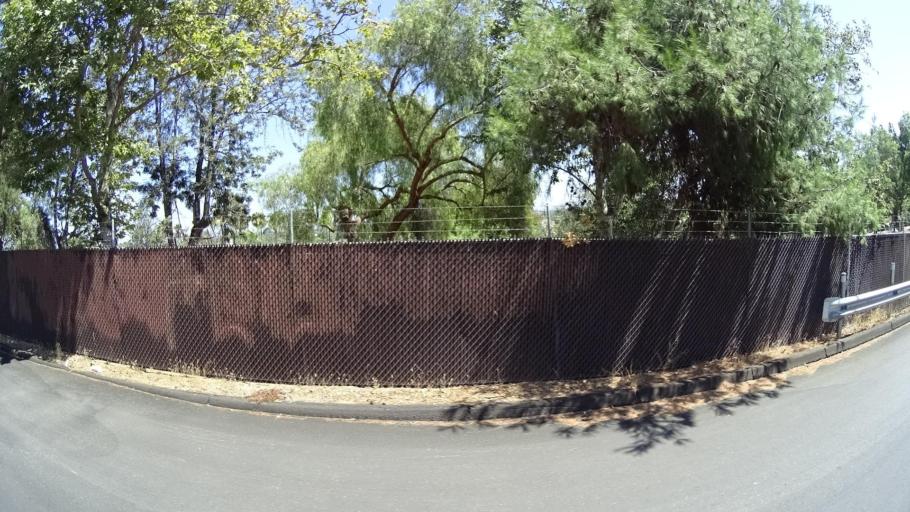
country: US
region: California
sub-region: San Diego County
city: Fallbrook
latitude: 33.3623
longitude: -117.2537
